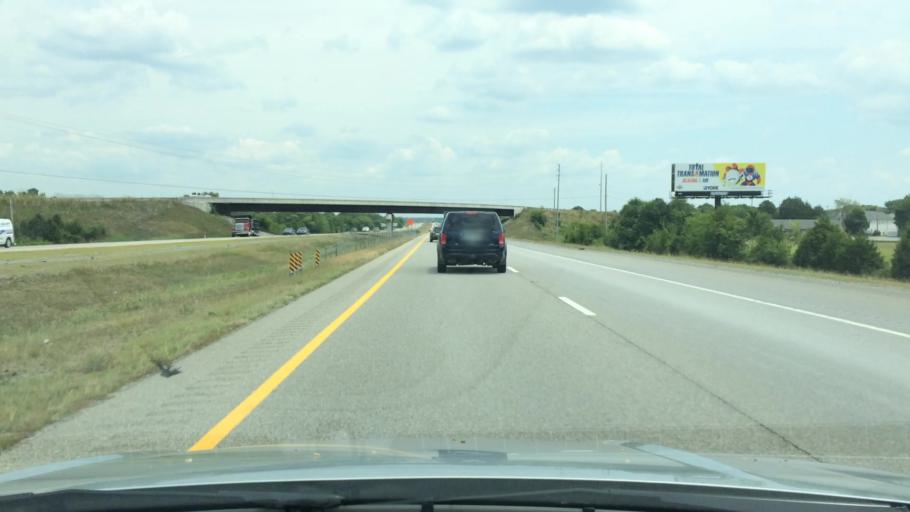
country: US
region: Tennessee
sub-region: Rutherford County
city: Murfreesboro
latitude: 35.8735
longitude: -86.4949
